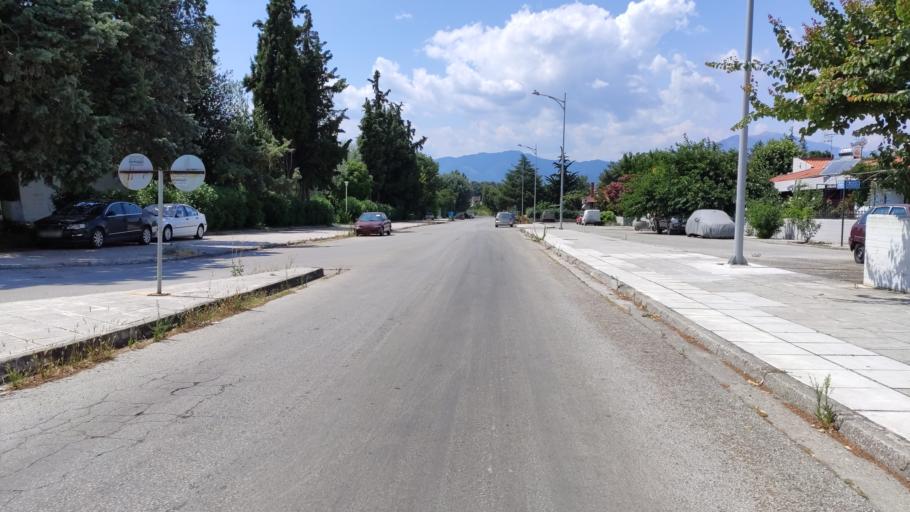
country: GR
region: East Macedonia and Thrace
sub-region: Nomos Rodopis
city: Komotini
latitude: 41.1210
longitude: 25.3918
